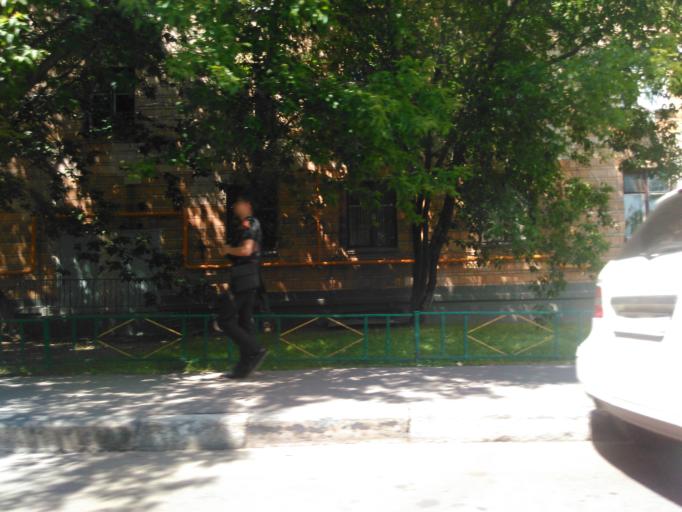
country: RU
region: Moskovskaya
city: Semenovskoye
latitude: 55.6907
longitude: 37.5392
